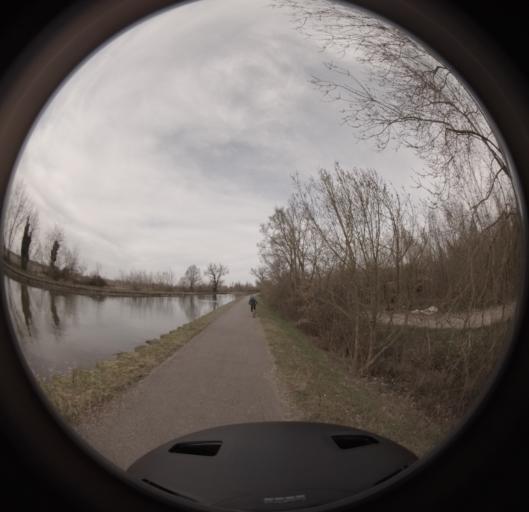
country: FR
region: Midi-Pyrenees
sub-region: Departement du Tarn-et-Garonne
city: Montech
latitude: 43.9787
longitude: 1.2504
